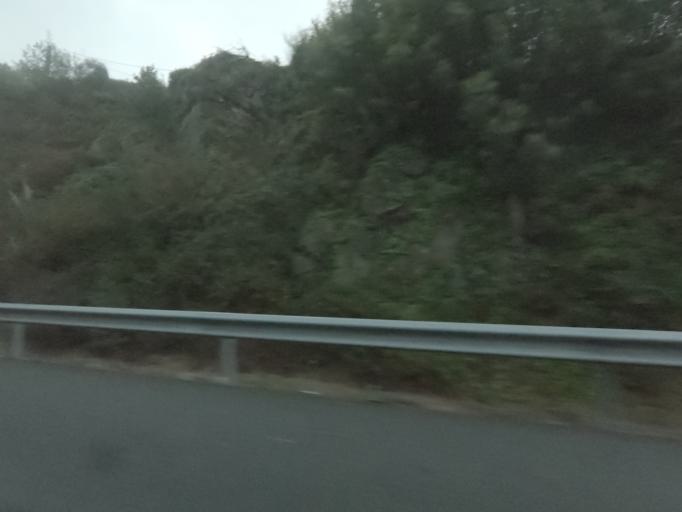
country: ES
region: Galicia
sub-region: Provincia de Pontevedra
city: Redondela
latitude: 42.3315
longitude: -8.6483
